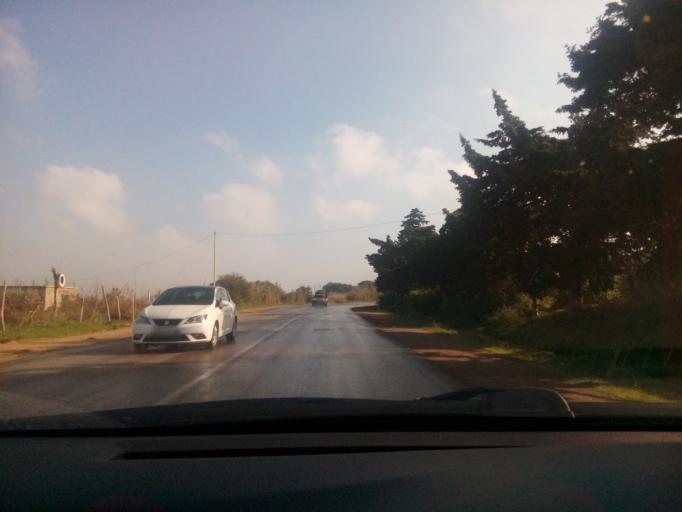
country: DZ
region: Oran
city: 'Ain el Turk
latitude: 35.7047
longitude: -0.8283
